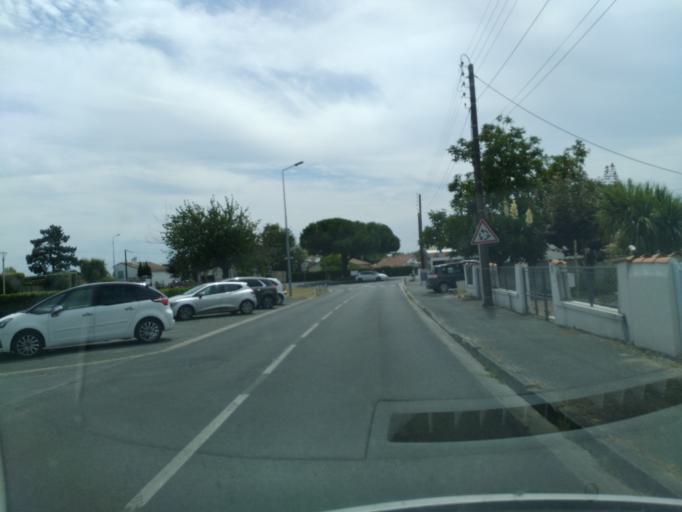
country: FR
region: Poitou-Charentes
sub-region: Departement de la Charente-Maritime
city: Saint-Palais-sur-Mer
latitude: 45.6538
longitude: -1.0785
